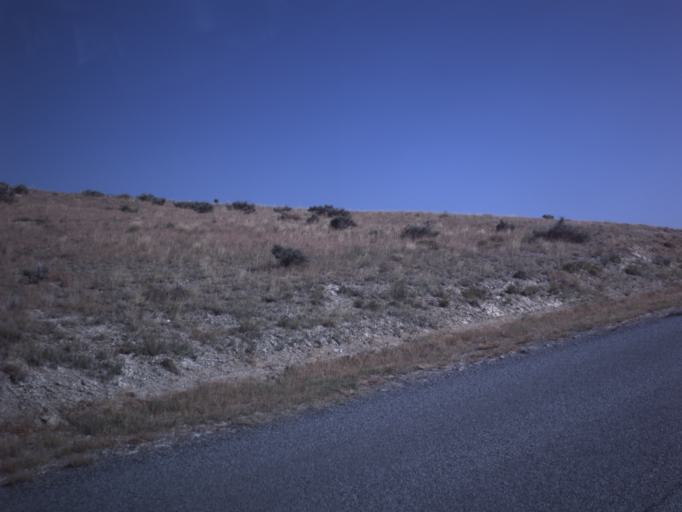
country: US
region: Utah
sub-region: Millard County
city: Fillmore
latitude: 38.9073
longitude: -112.8185
